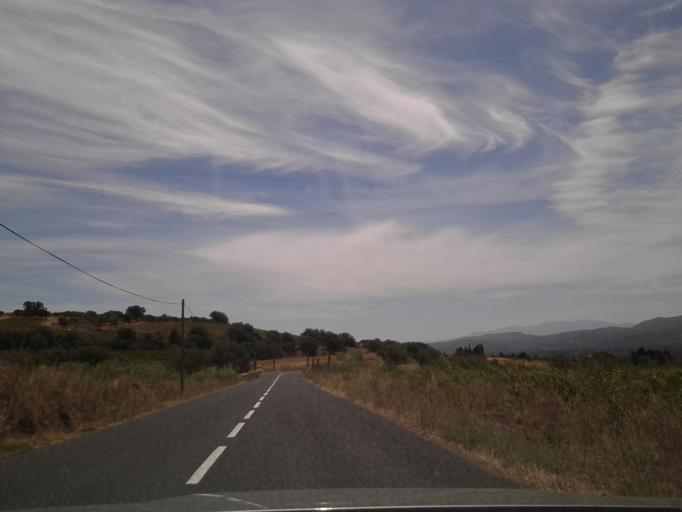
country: FR
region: Languedoc-Roussillon
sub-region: Departement des Pyrenees-Orientales
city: Millas
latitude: 42.7133
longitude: 2.6826
